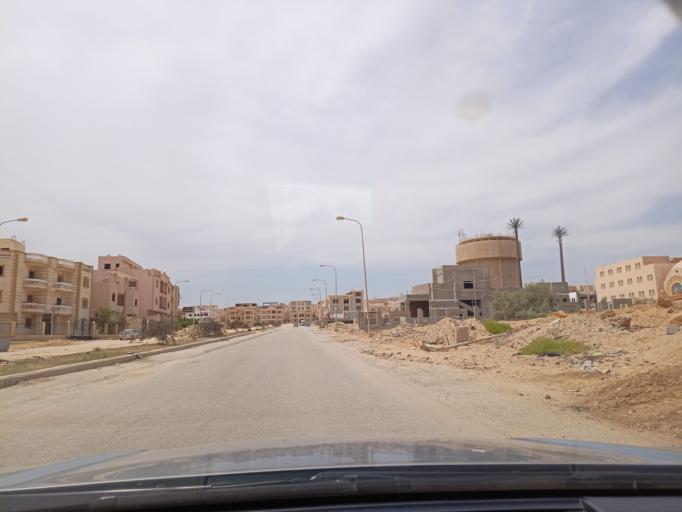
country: EG
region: Muhafazat al Qalyubiyah
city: Al Khankah
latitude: 30.2336
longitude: 31.4912
